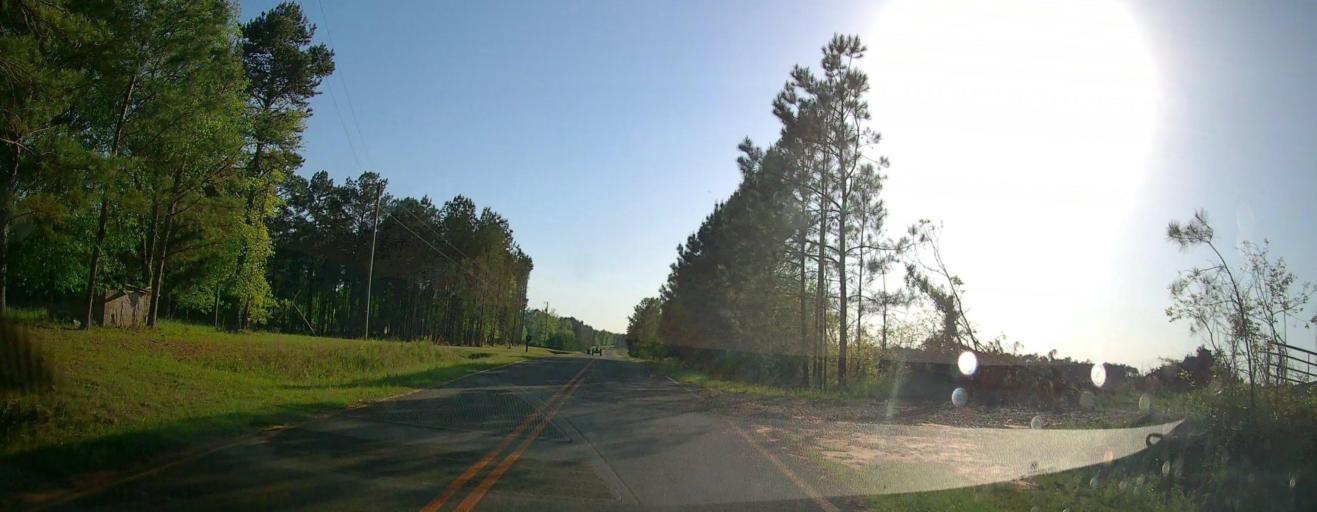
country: US
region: Georgia
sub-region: Macon County
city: Marshallville
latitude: 32.3923
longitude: -83.8440
